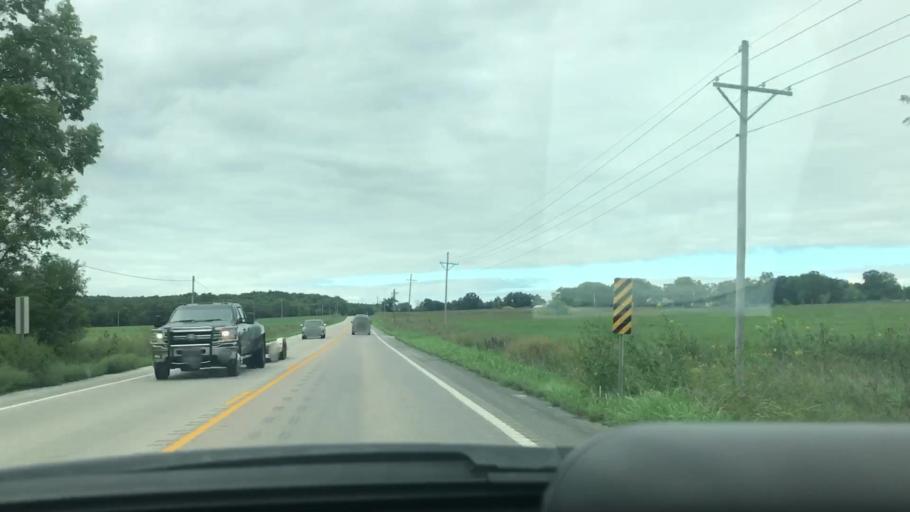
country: US
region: Missouri
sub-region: Hickory County
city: Hermitage
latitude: 37.8631
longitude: -93.1782
